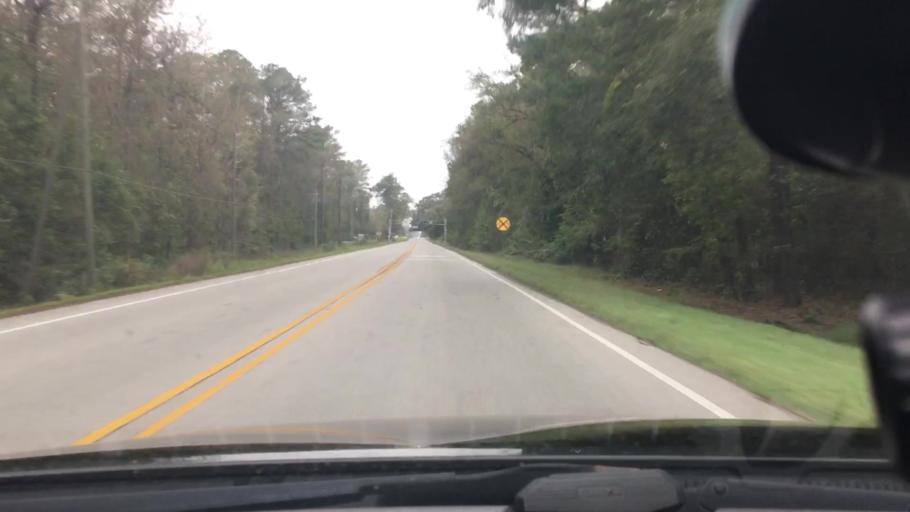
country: US
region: North Carolina
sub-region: Craven County
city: Vanceboro
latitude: 35.2363
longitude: -77.0741
